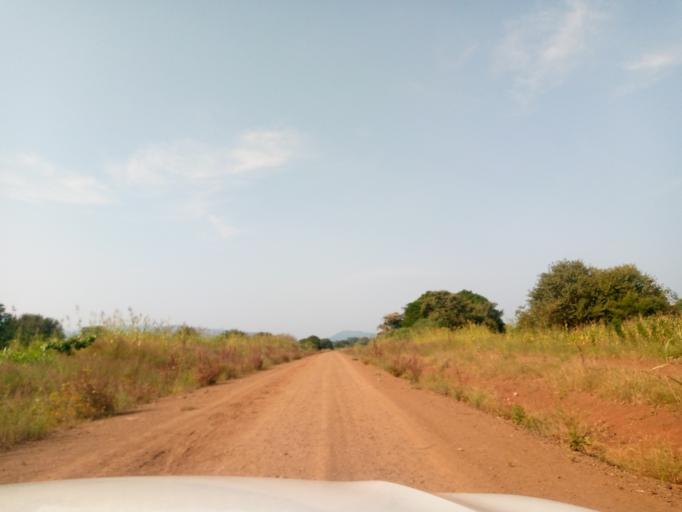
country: ET
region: Oromiya
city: Mendi
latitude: 10.1413
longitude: 34.9481
